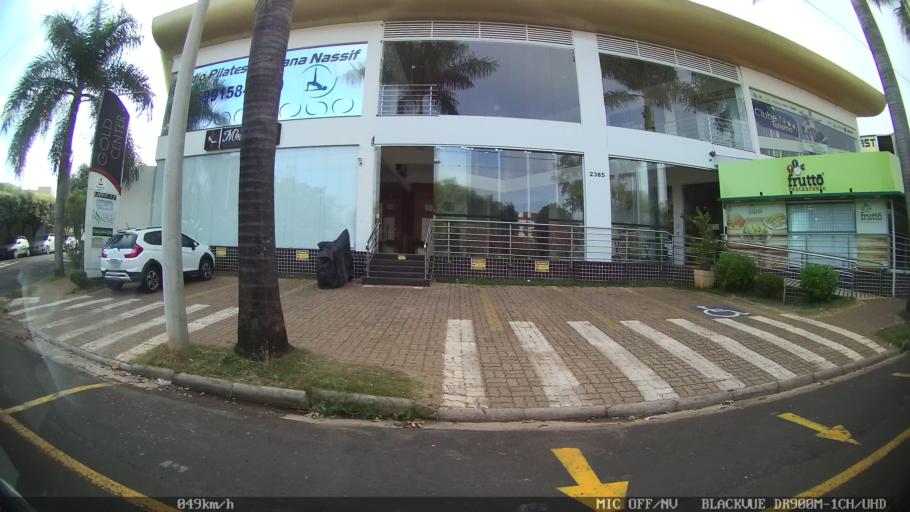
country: BR
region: Sao Paulo
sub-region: Sao Jose Do Rio Preto
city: Sao Jose do Rio Preto
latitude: -20.8327
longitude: -49.3653
